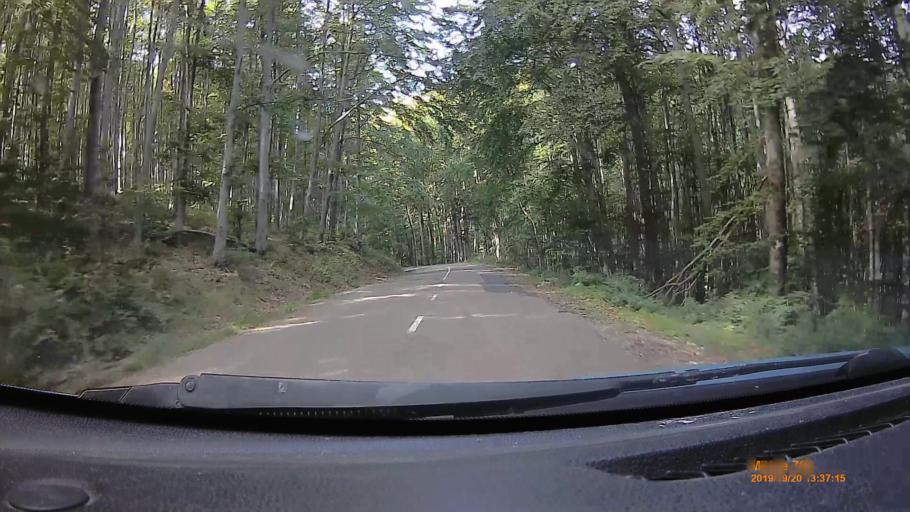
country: HU
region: Heves
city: Szilvasvarad
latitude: 48.0587
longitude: 20.5190
